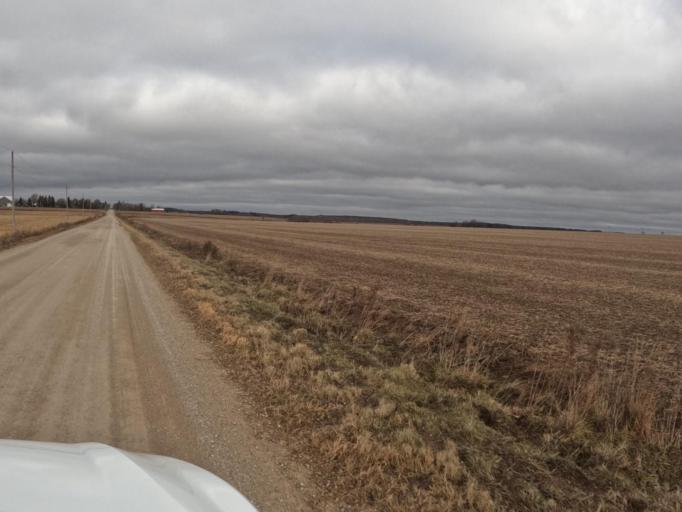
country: CA
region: Ontario
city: Shelburne
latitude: 44.0012
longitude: -80.4096
